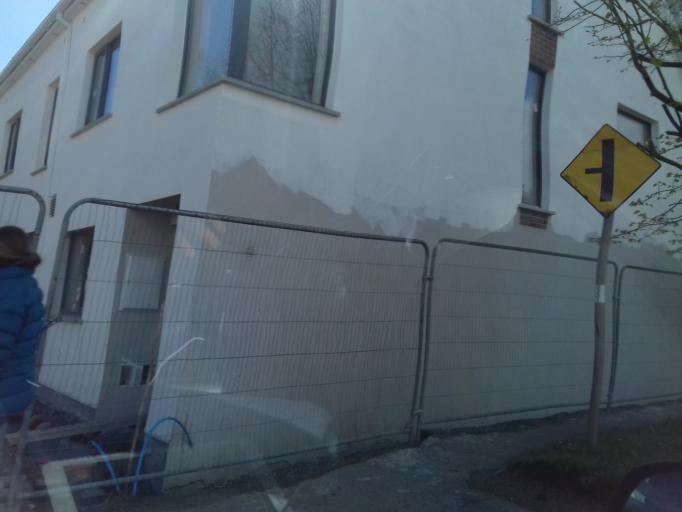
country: IE
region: Leinster
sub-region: Loch Garman
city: Castlebridge
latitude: 52.3807
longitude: -6.4503
